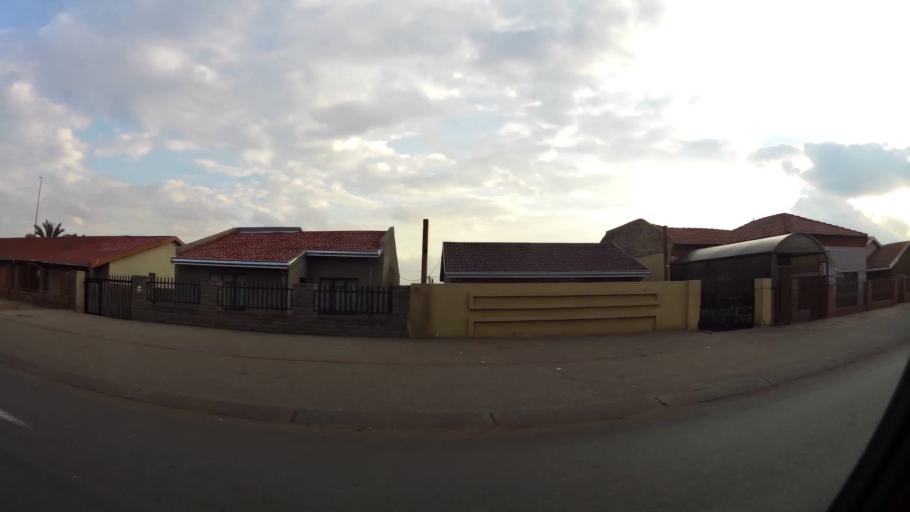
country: ZA
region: Gauteng
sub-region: City of Johannesburg Metropolitan Municipality
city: Orange Farm
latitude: -26.5733
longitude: 27.8388
